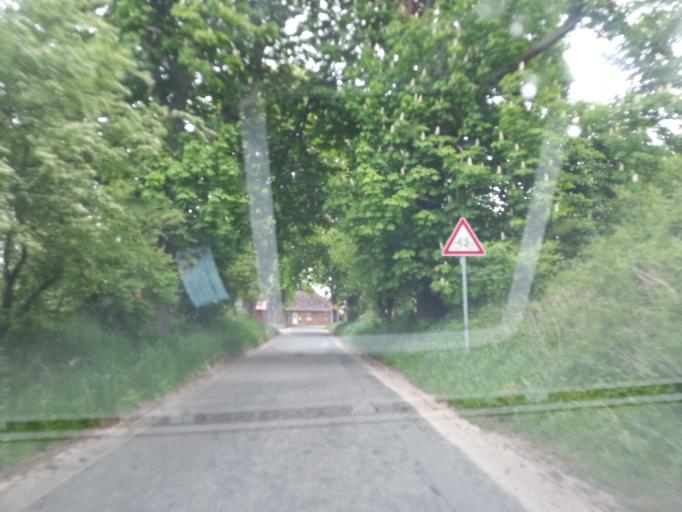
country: DE
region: Mecklenburg-Vorpommern
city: Malchow
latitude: 53.5156
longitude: 12.3775
